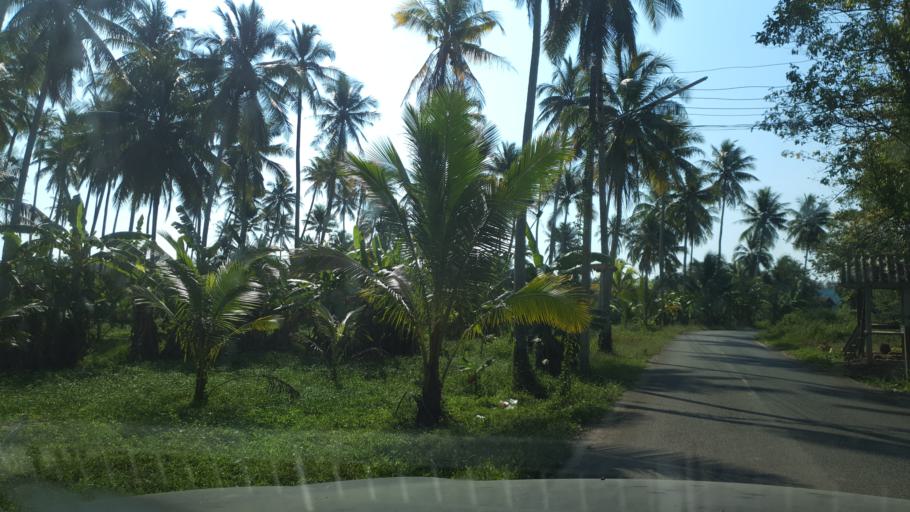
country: TH
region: Prachuap Khiri Khan
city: Thap Sakae
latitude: 11.3627
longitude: 99.5529
